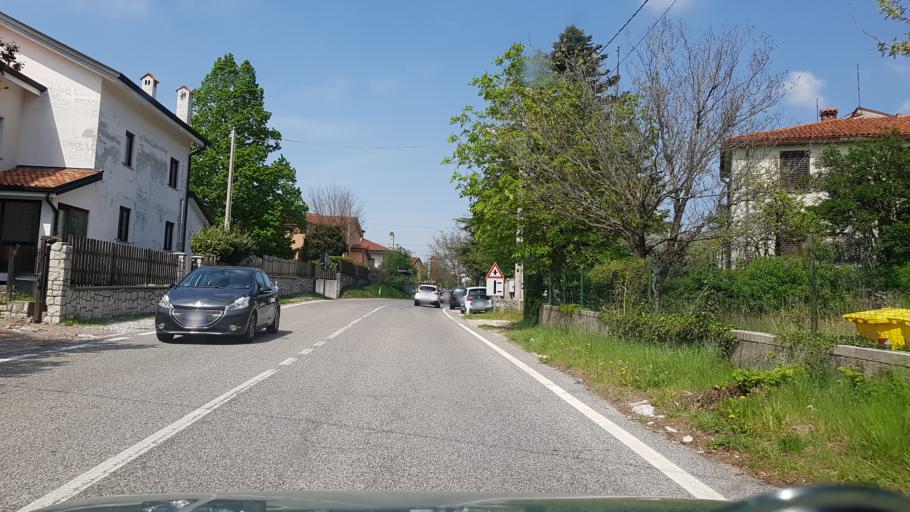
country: SI
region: Hrpelje-Kozina
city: Kozina
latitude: 45.6266
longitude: 13.8988
